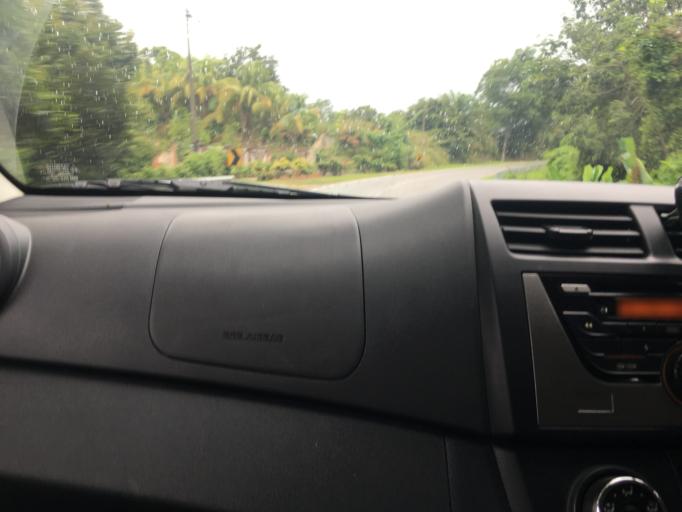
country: MY
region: Kedah
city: Bedong
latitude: 5.7103
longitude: 100.6316
